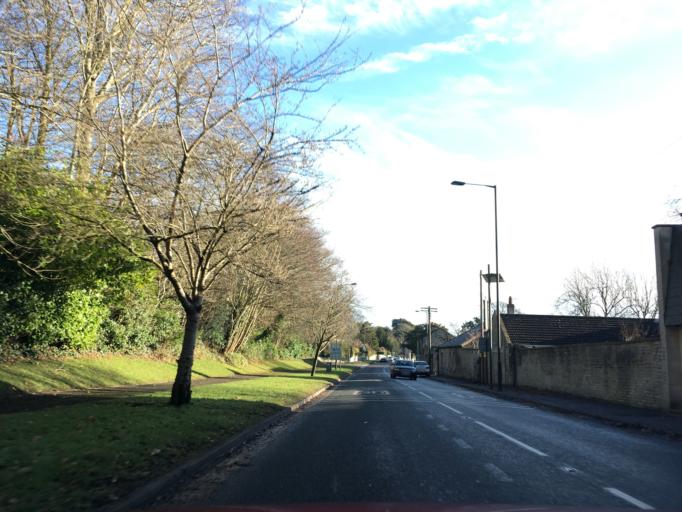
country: GB
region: England
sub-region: Bath and North East Somerset
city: Corston
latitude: 51.3918
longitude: -2.4037
